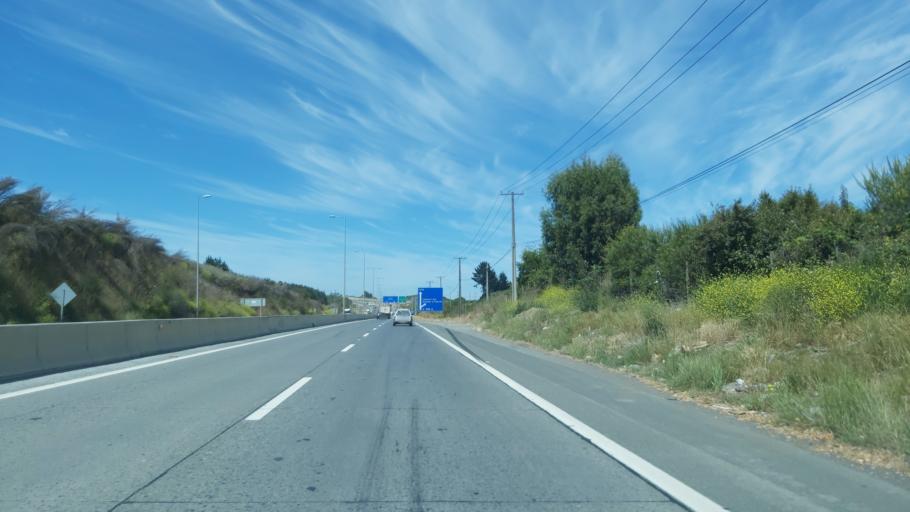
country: CL
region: Biobio
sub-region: Provincia de Concepcion
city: Coronel
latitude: -37.0412
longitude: -73.1368
